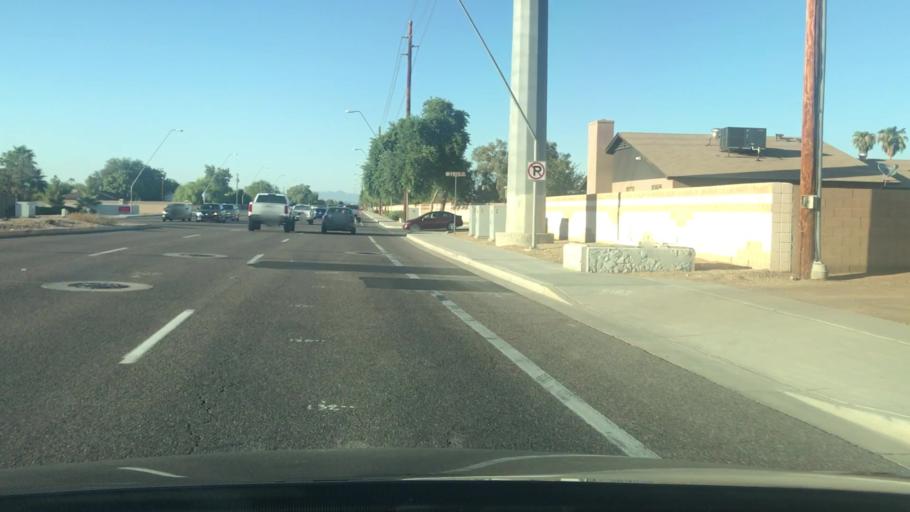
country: US
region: Arizona
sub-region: Maricopa County
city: Chandler
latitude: 33.2991
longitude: -111.8069
